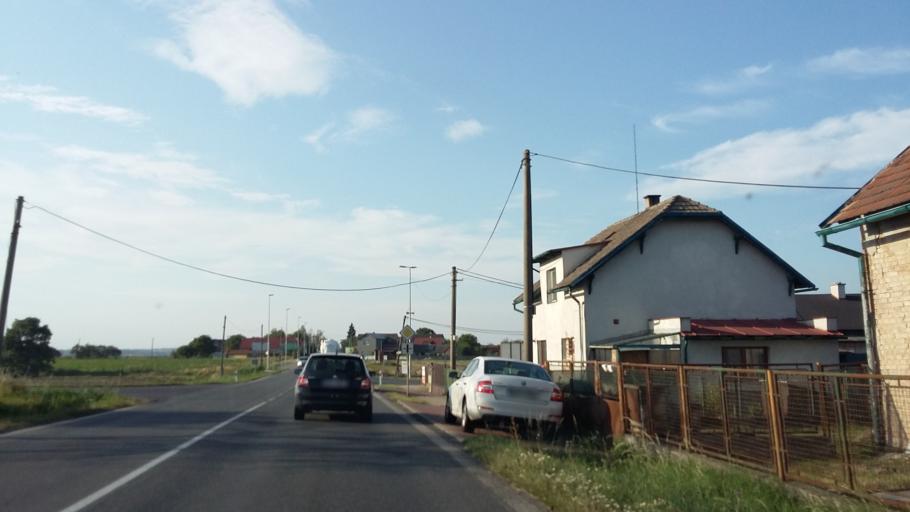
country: CZ
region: Central Bohemia
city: Lustenice
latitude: 50.3505
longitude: 14.9140
